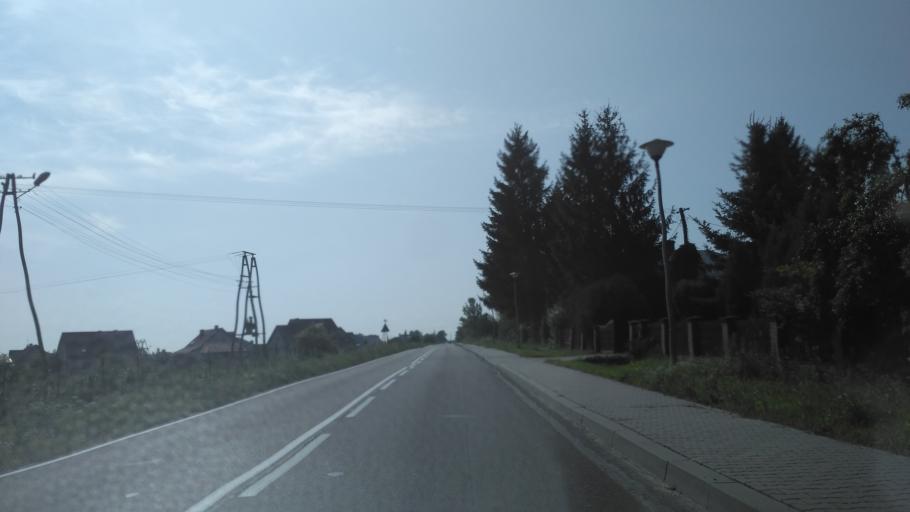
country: PL
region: Lublin Voivodeship
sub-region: Powiat leczynski
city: Cycow
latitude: 51.1894
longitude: 23.1636
